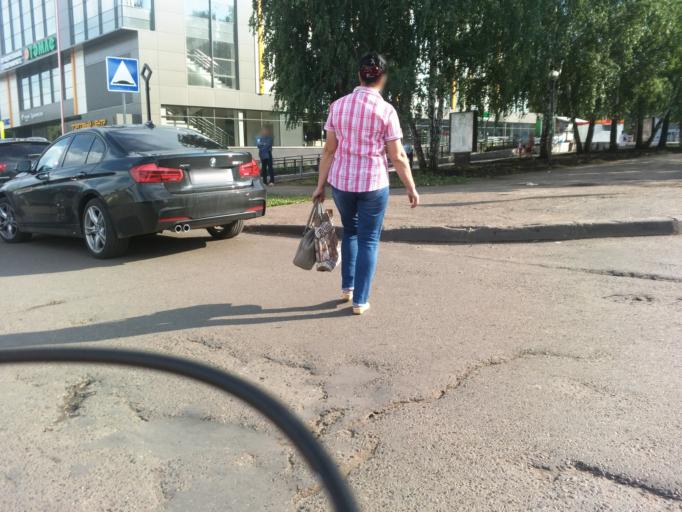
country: RU
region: Tatarstan
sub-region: Tukayevskiy Rayon
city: Naberezhnyye Chelny
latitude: 55.7455
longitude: 52.4229
